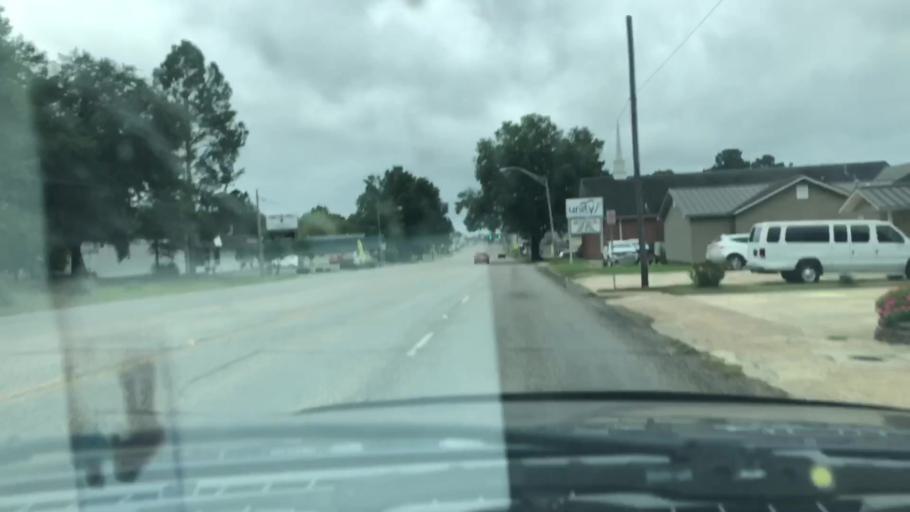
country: US
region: Arkansas
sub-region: Miller County
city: Texarkana
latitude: 33.4430
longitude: -94.0532
